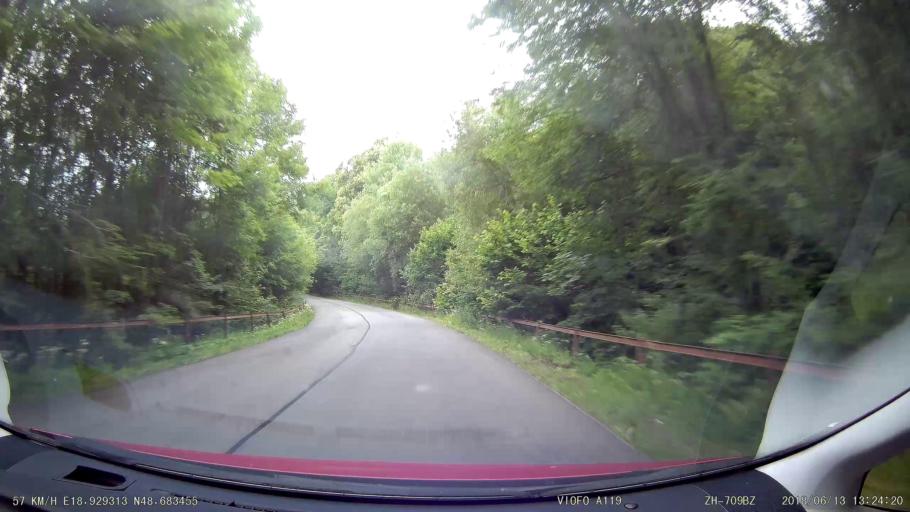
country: SK
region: Banskobystricky
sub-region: Okres Ziar nad Hronom
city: Kremnica
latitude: 48.6836
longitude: 18.9293
